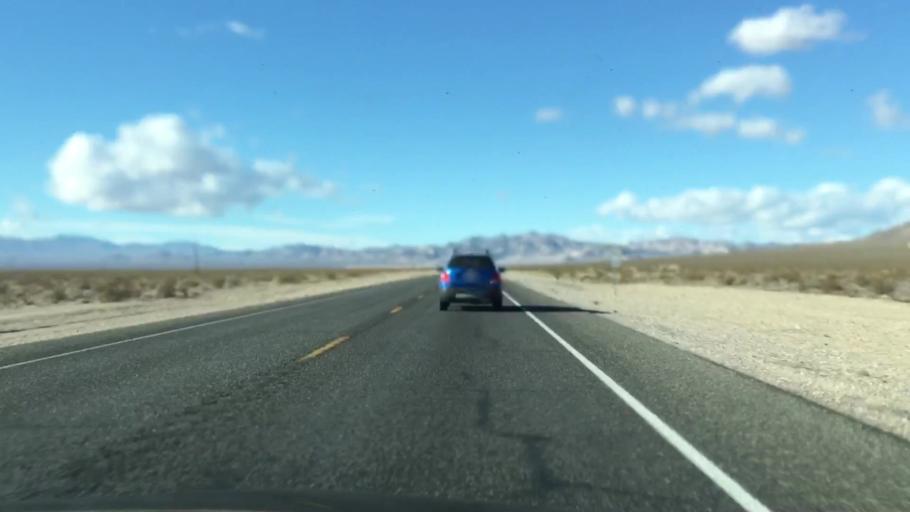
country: US
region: Nevada
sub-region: Nye County
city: Beatty
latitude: 36.7956
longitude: -116.7108
